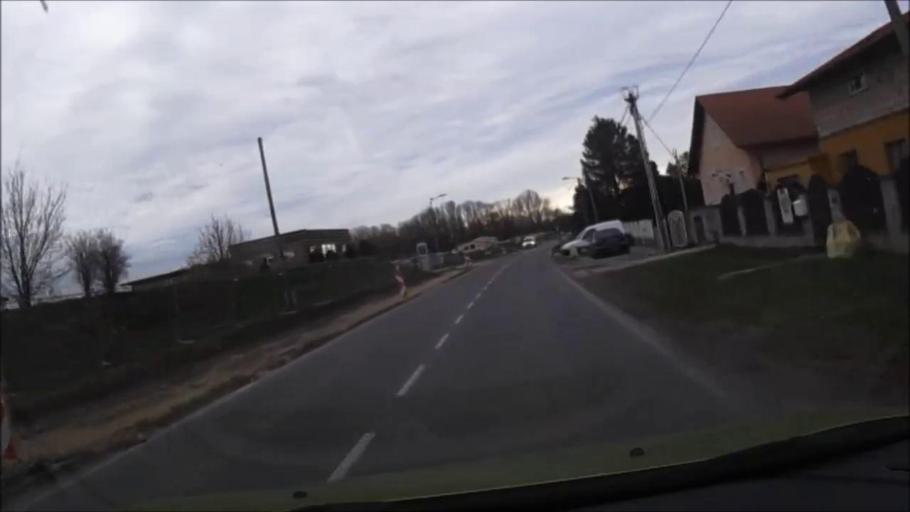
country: AT
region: Lower Austria
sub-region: Politischer Bezirk Baden
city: Ebreichsdorf
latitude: 47.9578
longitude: 16.4332
